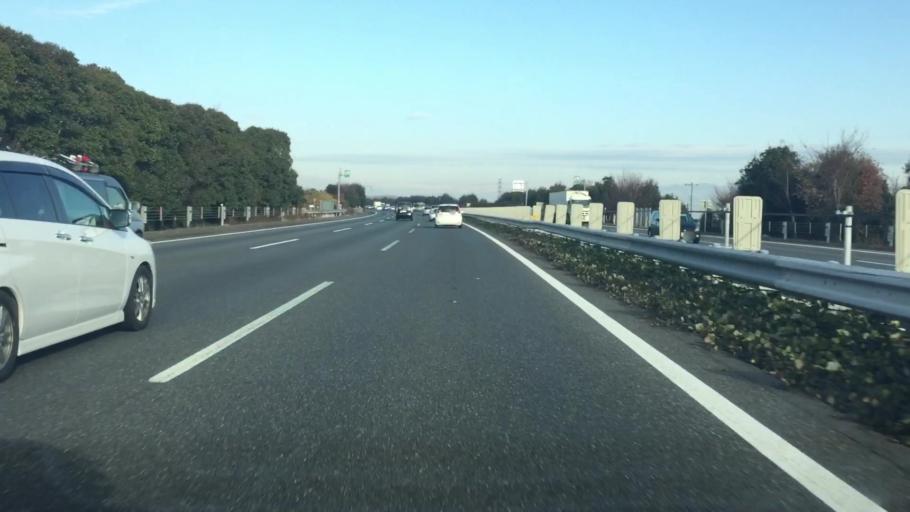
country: JP
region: Saitama
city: Honjo
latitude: 36.1906
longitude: 139.1895
